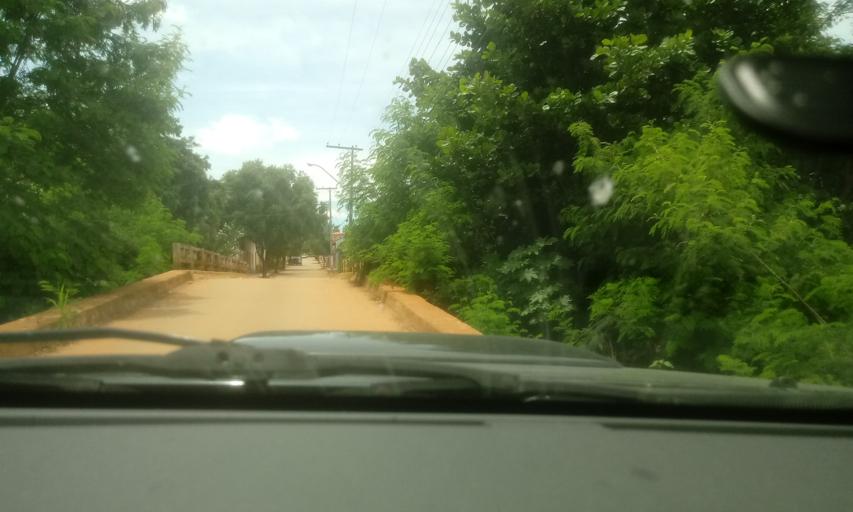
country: BR
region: Bahia
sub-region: Riacho De Santana
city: Riacho de Santana
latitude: -13.6072
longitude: -42.9442
